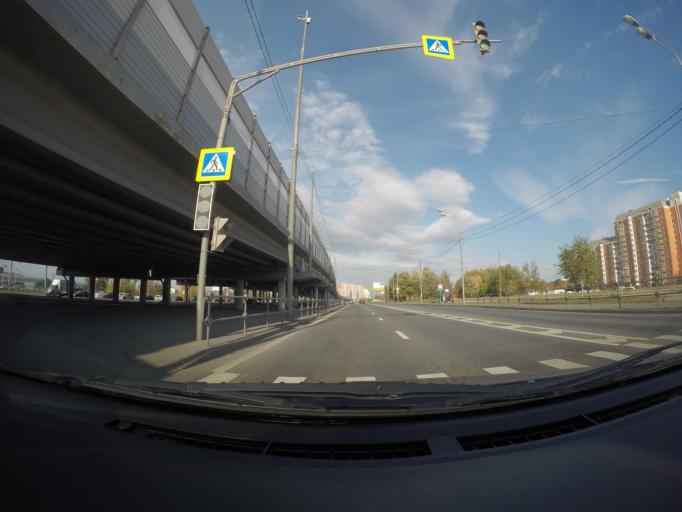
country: RU
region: Moscow
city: Vagonoremont
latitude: 55.9132
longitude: 37.5450
